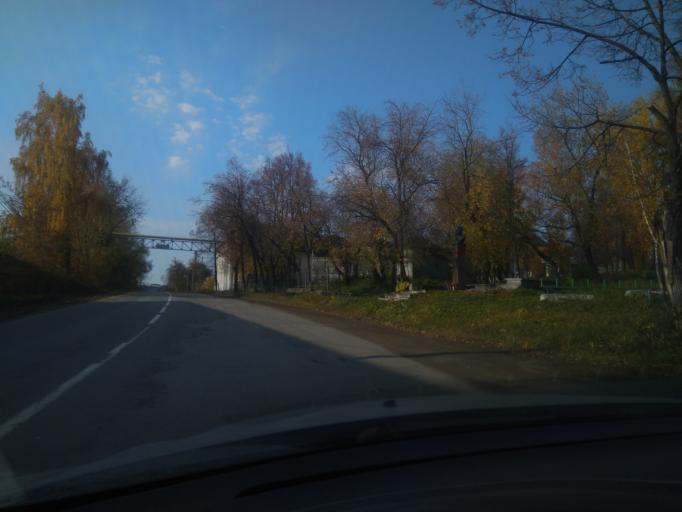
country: RU
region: Sverdlovsk
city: Nizhniye Sergi
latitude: 56.6685
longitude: 59.3186
